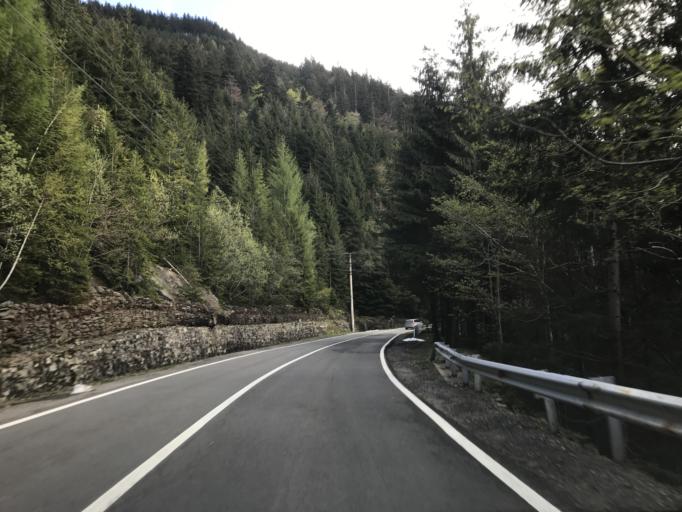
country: RO
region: Sibiu
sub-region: Comuna Cartisoara
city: Cartisoara
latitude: 45.6521
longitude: 24.6044
